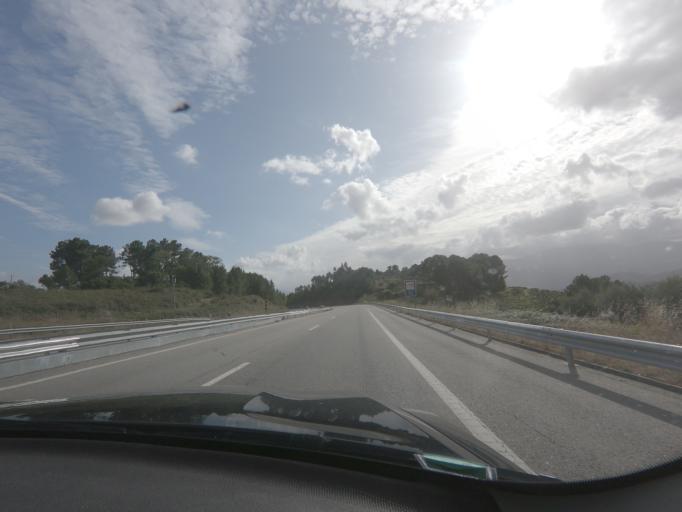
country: PT
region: Vila Real
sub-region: Vila Real
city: Vila Real
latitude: 41.2434
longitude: -7.7230
